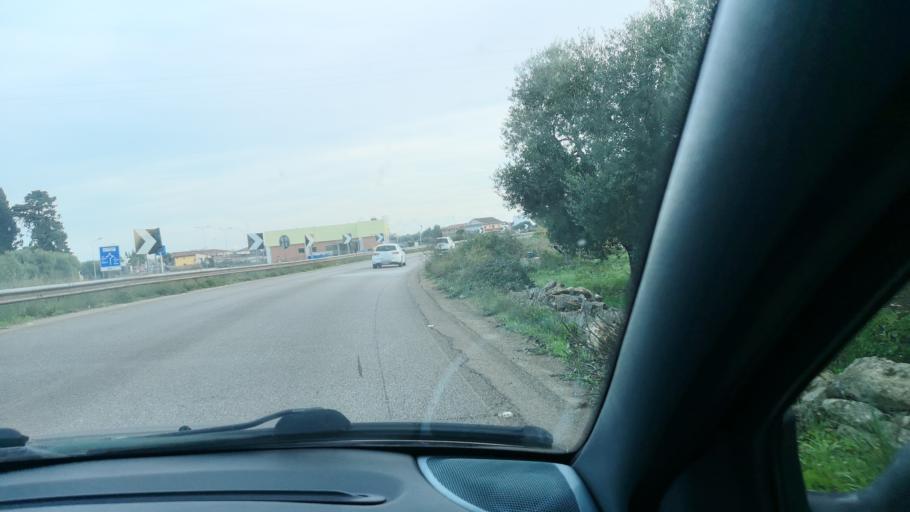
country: IT
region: Apulia
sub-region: Provincia di Bari
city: Sannicandro di Bari
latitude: 40.9903
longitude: 16.7974
